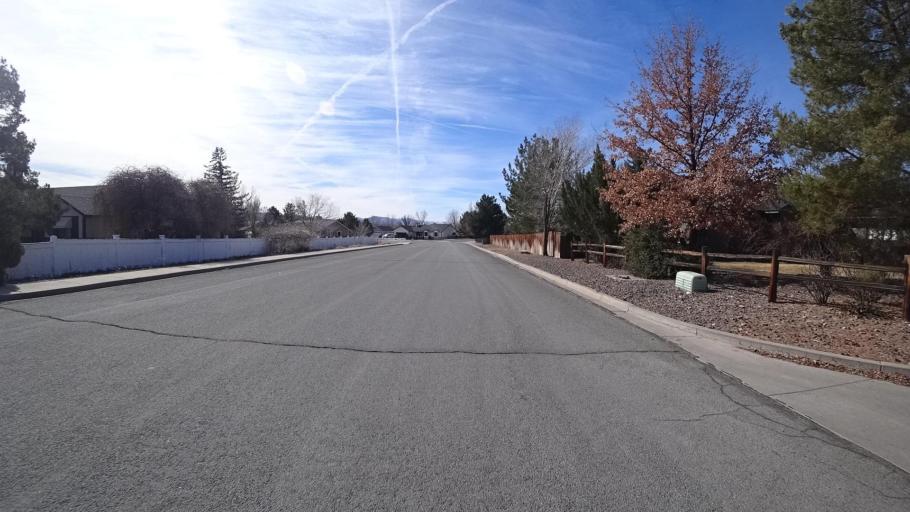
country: US
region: Nevada
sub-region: Washoe County
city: Spanish Springs
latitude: 39.6254
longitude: -119.7251
